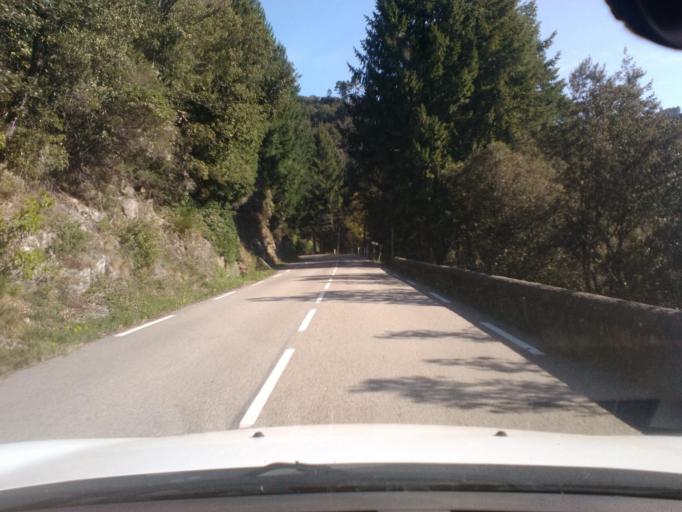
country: FR
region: Languedoc-Roussillon
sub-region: Departement du Gard
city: Saint-Jean-du-Gard
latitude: 44.1080
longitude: 3.8115
